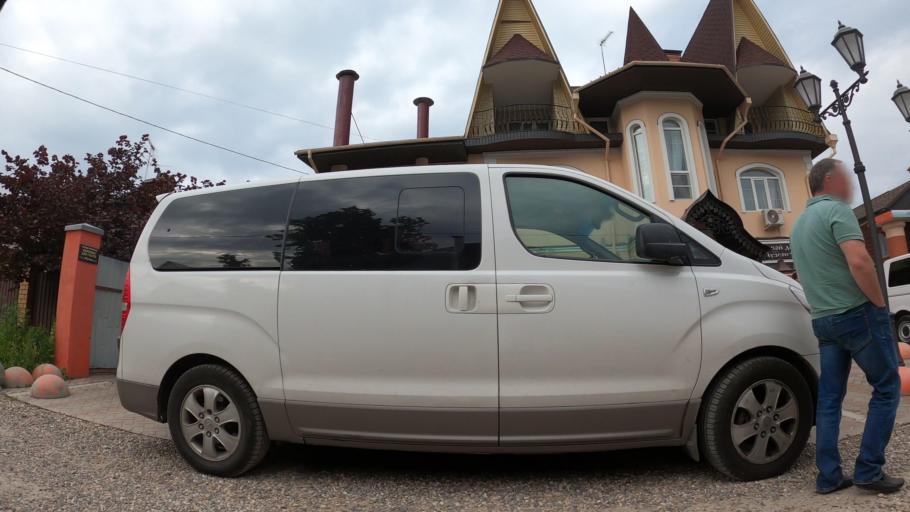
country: RU
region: Moskovskaya
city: Ivanteyevka
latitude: 55.9672
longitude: 37.9201
